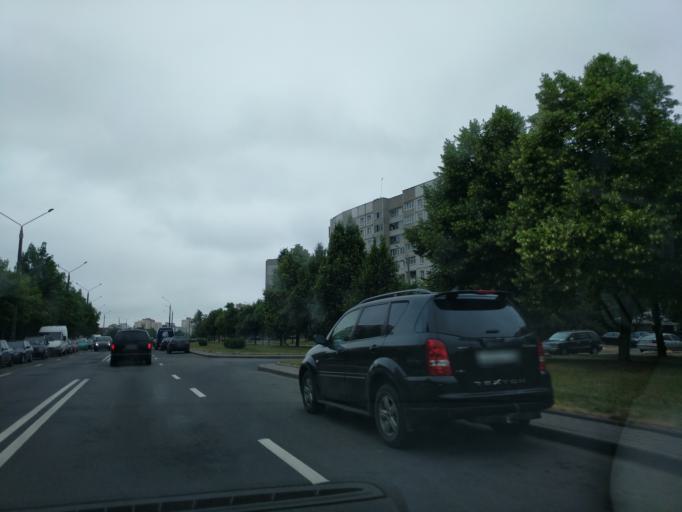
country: BY
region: Minsk
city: Malinovka
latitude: 53.8579
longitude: 27.4586
